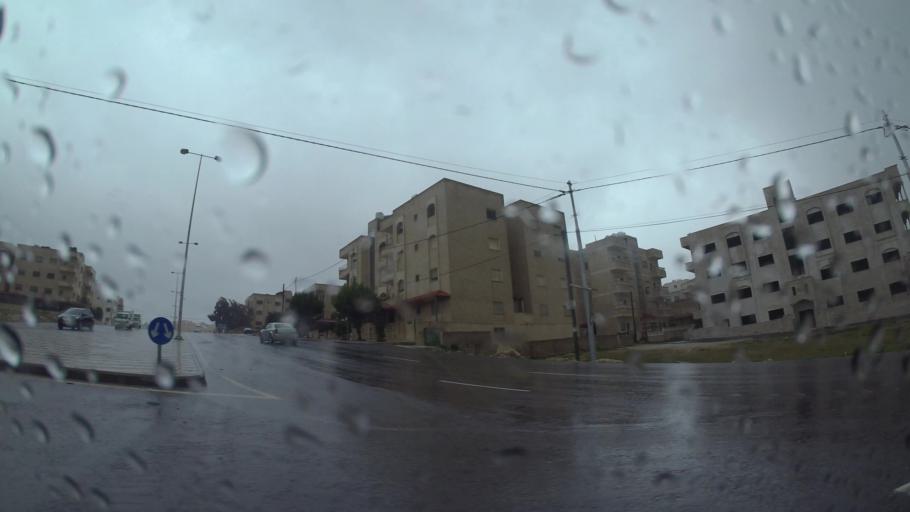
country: JO
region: Amman
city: Al Jubayhah
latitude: 32.0345
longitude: 35.8831
